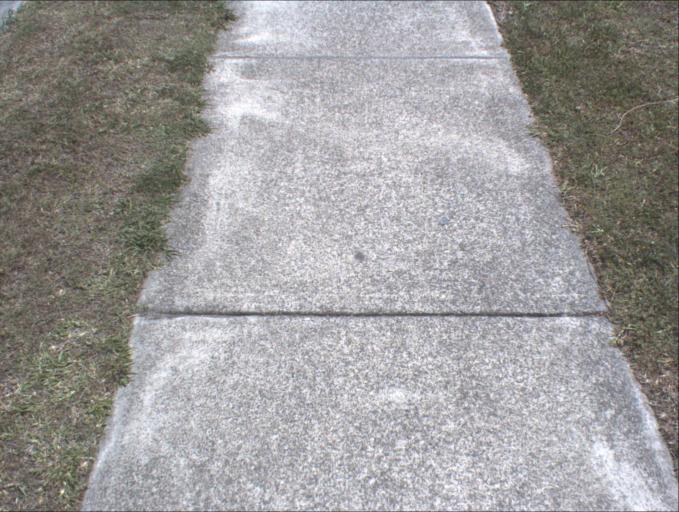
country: AU
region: Queensland
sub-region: Logan
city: Windaroo
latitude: -27.7314
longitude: 153.2065
